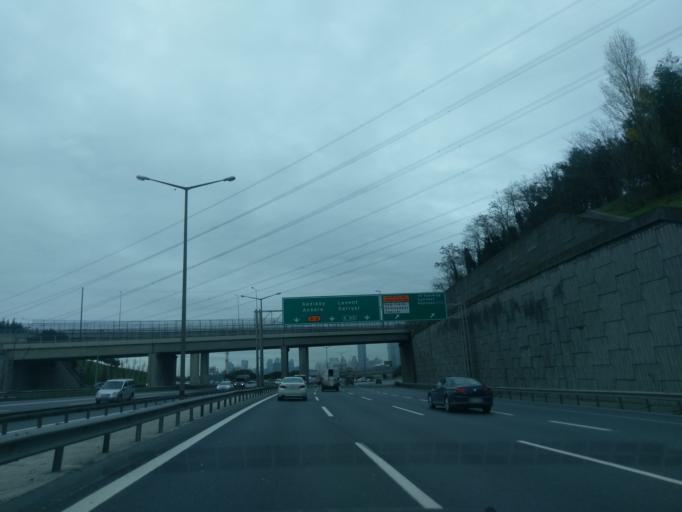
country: TR
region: Istanbul
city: Sisli
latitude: 41.0993
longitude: 28.9569
